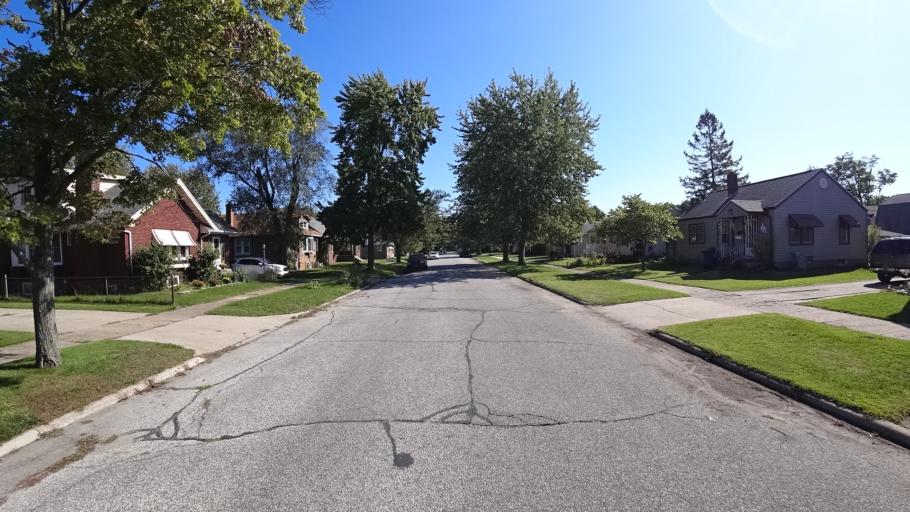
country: US
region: Indiana
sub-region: LaPorte County
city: Michigan City
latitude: 41.7075
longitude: -86.8873
